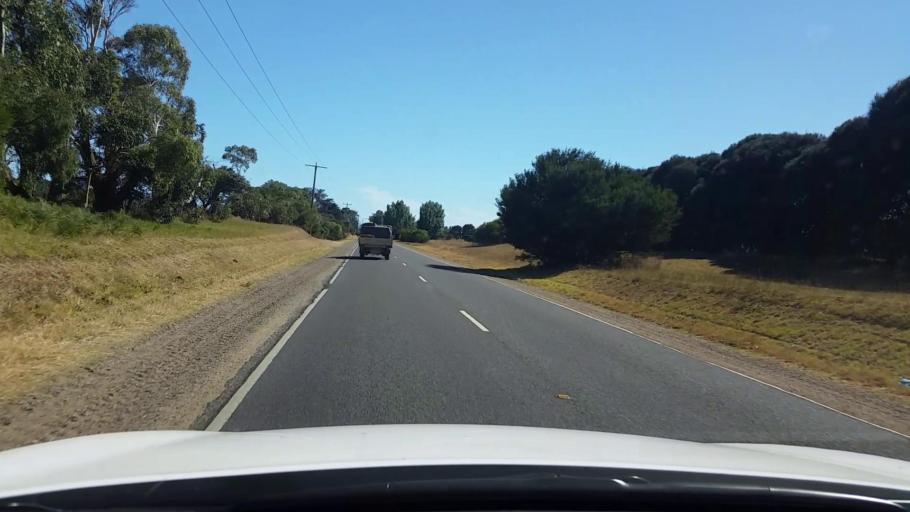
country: AU
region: Victoria
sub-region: Mornington Peninsula
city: Rosebud West
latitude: -38.4019
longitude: 144.8879
